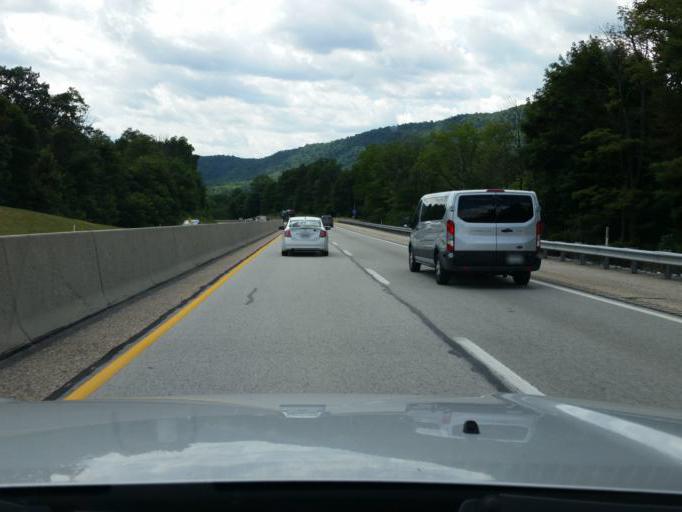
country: US
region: Pennsylvania
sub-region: Franklin County
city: Doylestown
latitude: 40.1585
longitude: -77.7013
